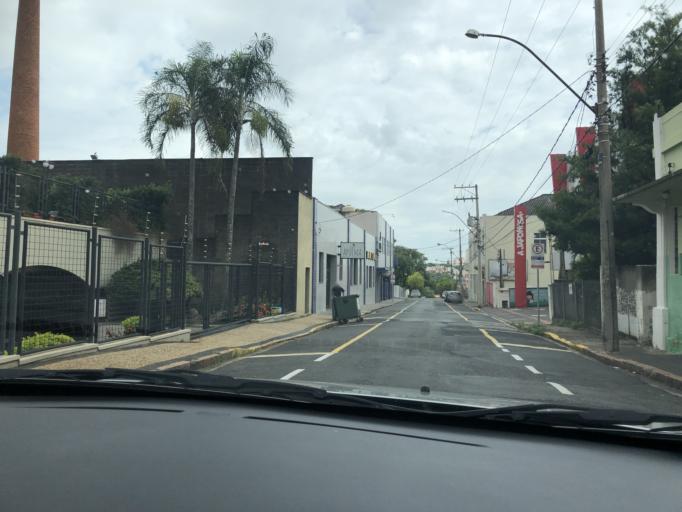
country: BR
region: Sao Paulo
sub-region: Americana
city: Americana
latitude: -22.7388
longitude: -47.3340
